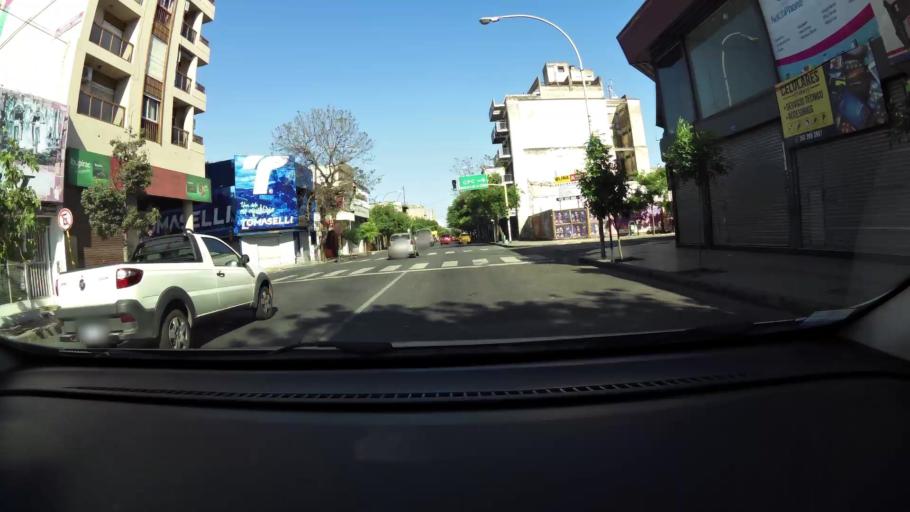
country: AR
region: Cordoba
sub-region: Departamento de Capital
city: Cordoba
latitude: -31.4108
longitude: -64.1790
